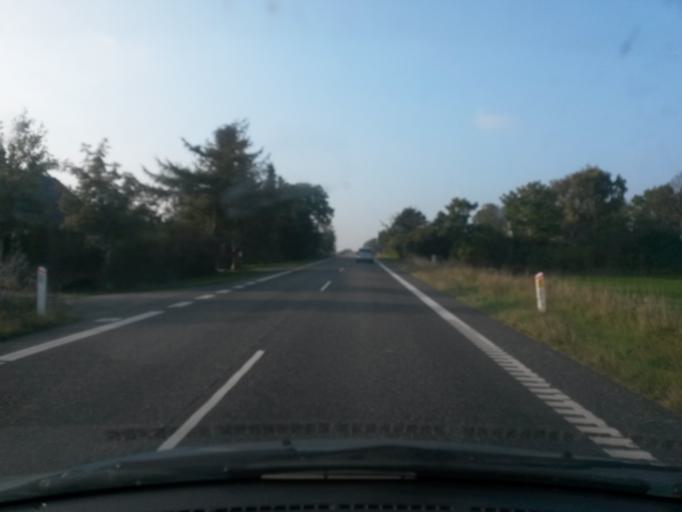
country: DK
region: Central Jutland
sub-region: Randers Kommune
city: Assentoft
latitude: 56.4308
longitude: 10.1939
